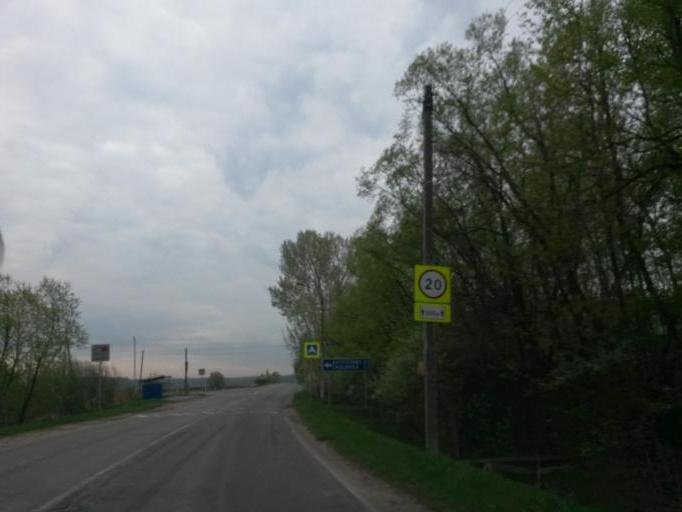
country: RU
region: Moskovskaya
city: Lyubuchany
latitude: 55.2474
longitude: 37.6395
